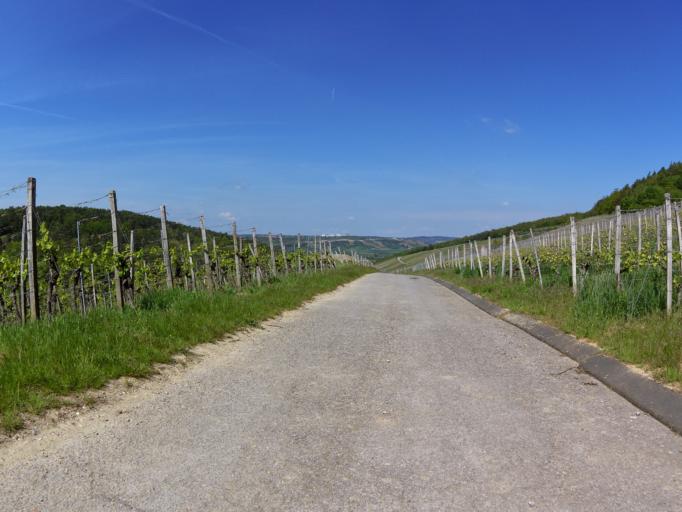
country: DE
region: Bavaria
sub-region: Regierungsbezirk Unterfranken
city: Eibelstadt
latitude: 49.7327
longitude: 10.0179
